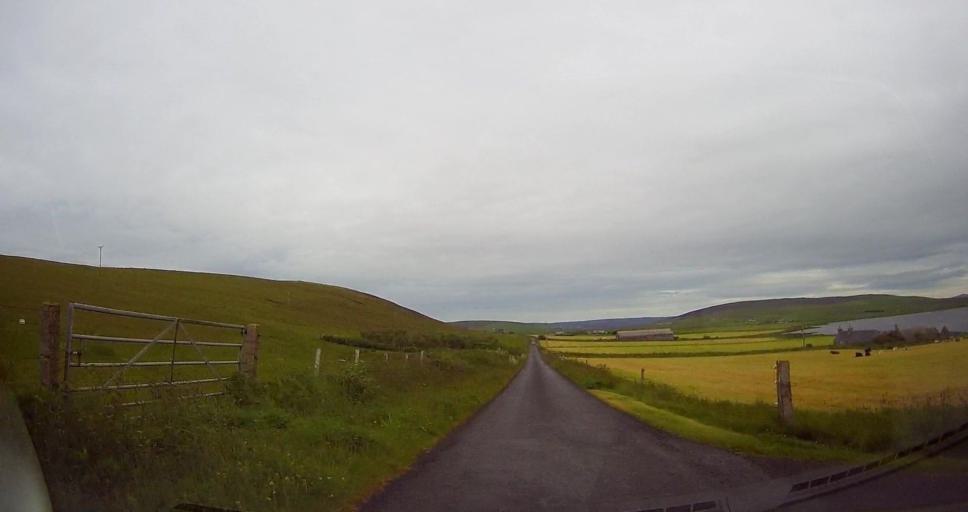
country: GB
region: Scotland
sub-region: Orkney Islands
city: Stromness
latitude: 59.1194
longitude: -3.2708
